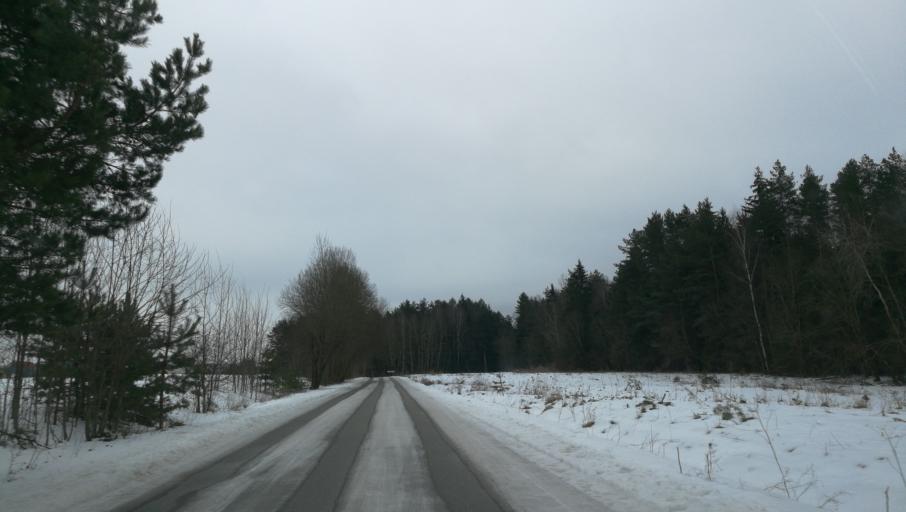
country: LT
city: Trakai
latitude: 54.6177
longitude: 24.9097
